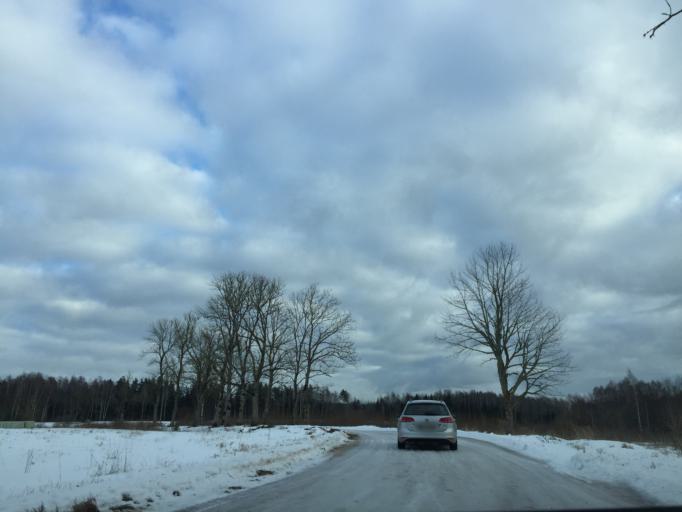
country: LV
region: Lielvarde
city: Lielvarde
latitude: 56.5833
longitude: 24.7346
